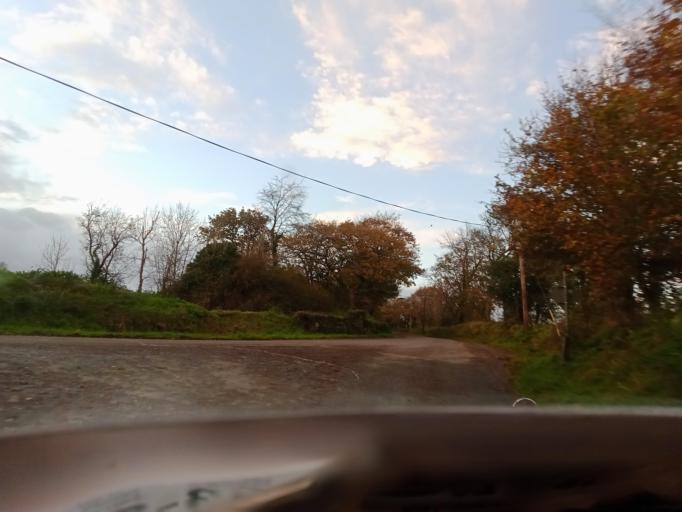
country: IE
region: Leinster
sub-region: Loch Garman
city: New Ross
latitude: 52.3393
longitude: -7.0130
